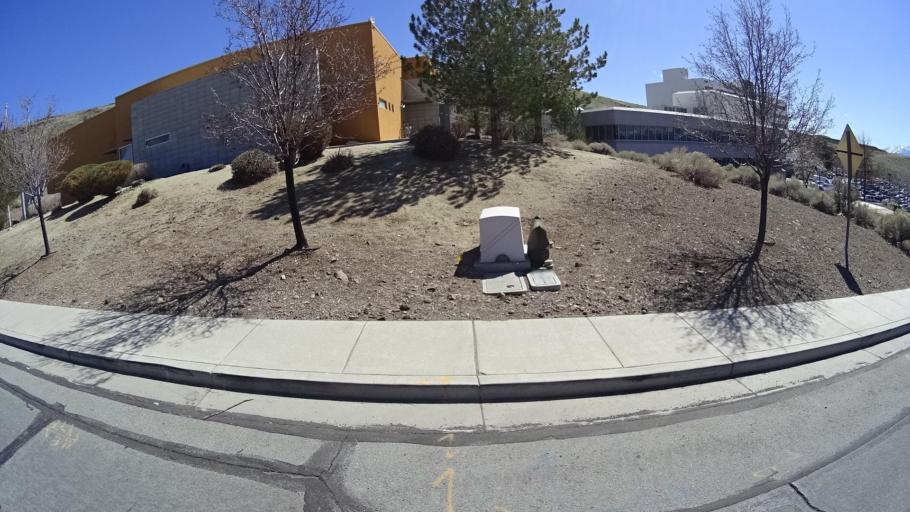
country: US
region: Nevada
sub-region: Washoe County
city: Sparks
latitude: 39.5426
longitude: -119.6971
